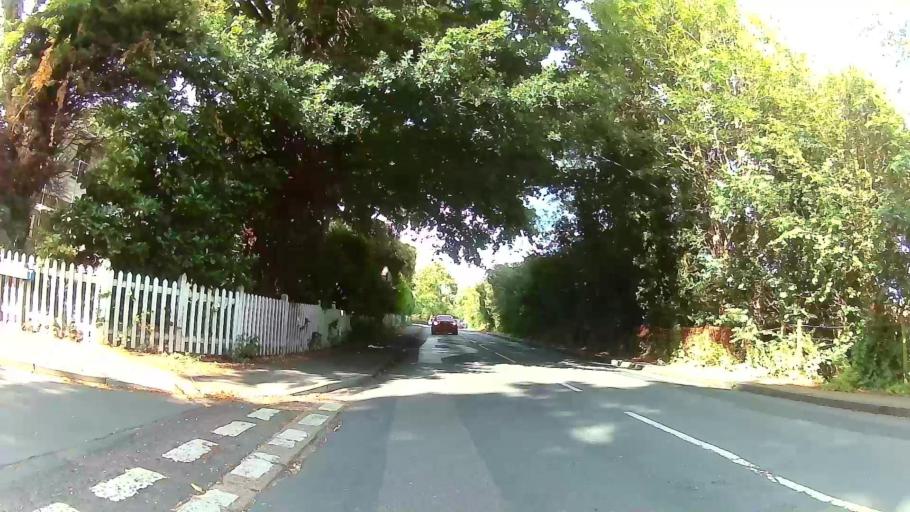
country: GB
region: England
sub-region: Greater London
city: Hainault
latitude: 51.6156
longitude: 0.0985
